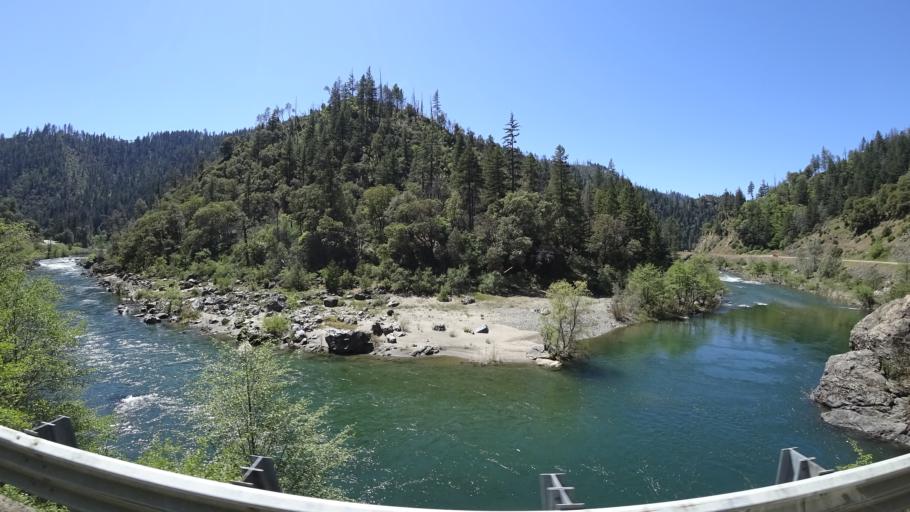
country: US
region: California
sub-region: Trinity County
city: Hayfork
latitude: 40.7609
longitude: -123.2819
